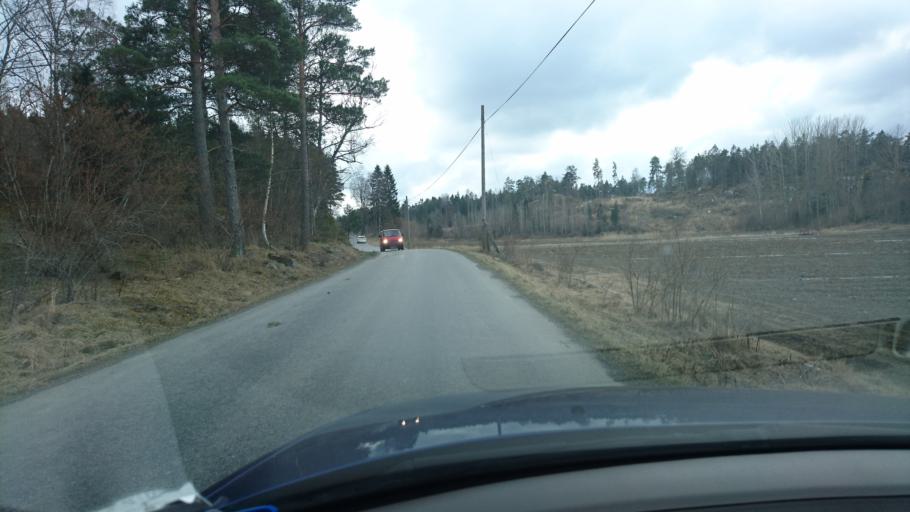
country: SE
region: Stockholm
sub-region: Norrtalje Kommun
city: Bjorko
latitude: 59.7993
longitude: 18.9678
